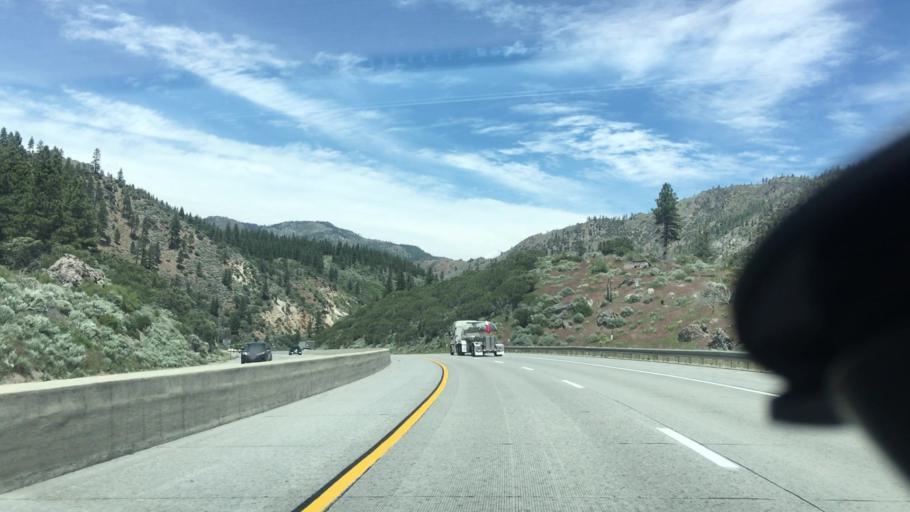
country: US
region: Nevada
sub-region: Washoe County
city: Verdi
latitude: 39.3887
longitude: -120.0246
